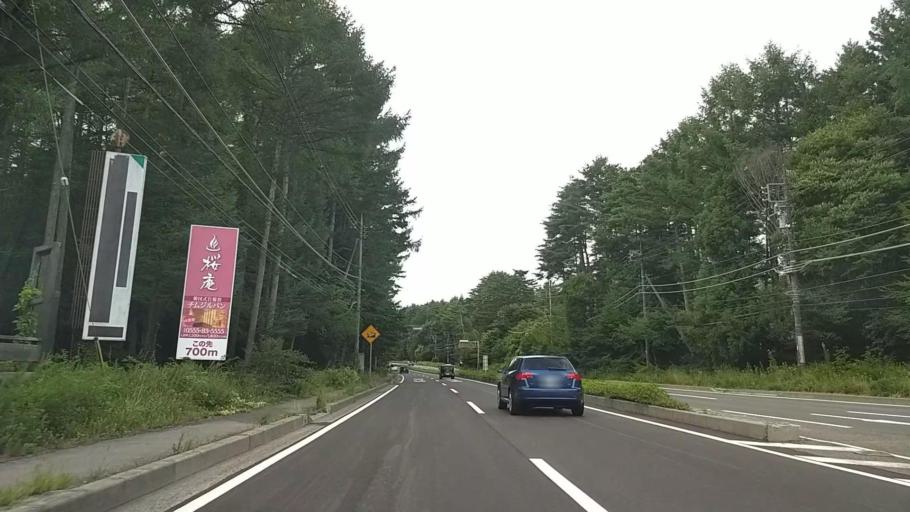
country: JP
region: Yamanashi
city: Fujikawaguchiko
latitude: 35.4889
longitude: 138.7393
